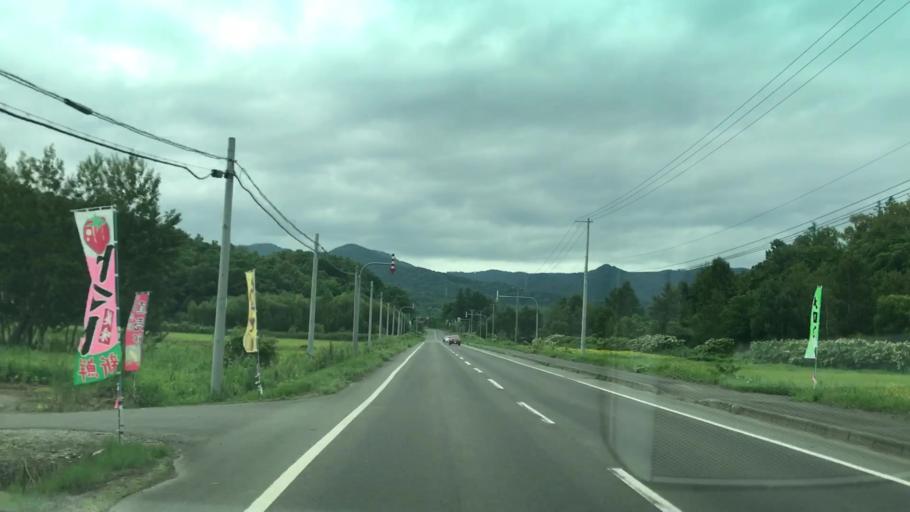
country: JP
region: Hokkaido
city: Yoichi
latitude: 43.0574
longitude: 140.8210
